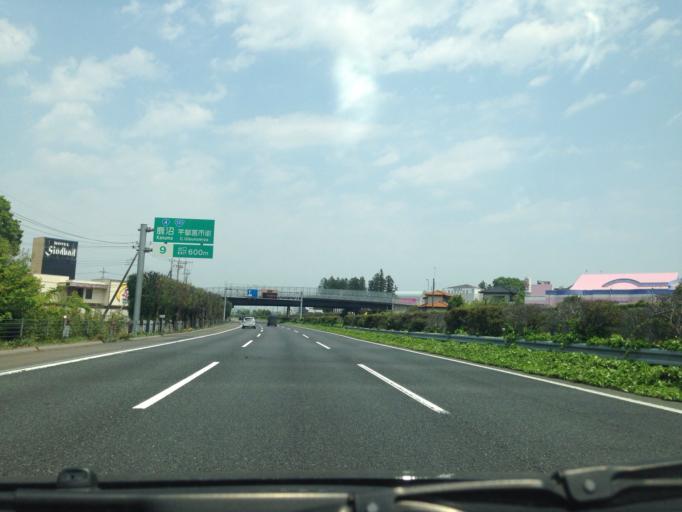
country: JP
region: Tochigi
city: Kanuma
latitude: 36.5331
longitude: 139.7949
